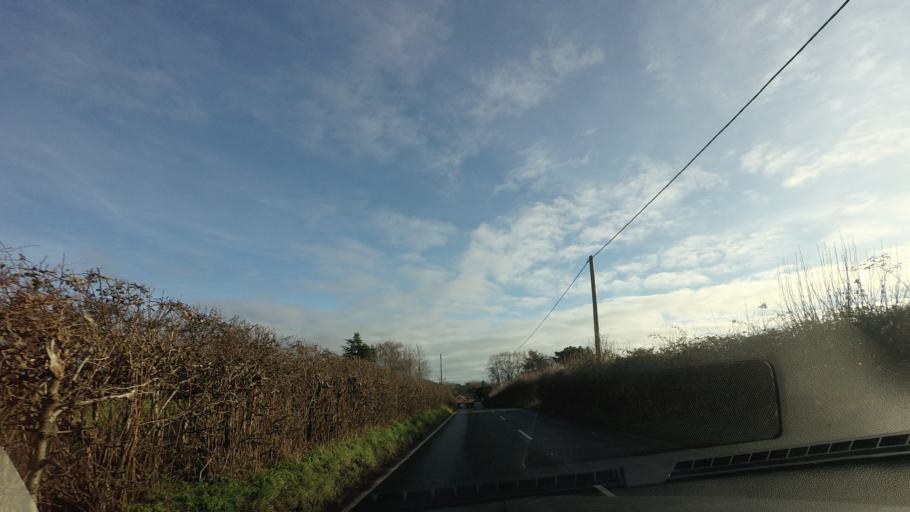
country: GB
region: England
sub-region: East Sussex
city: Bexhill-on-Sea
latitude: 50.8714
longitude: 0.4392
